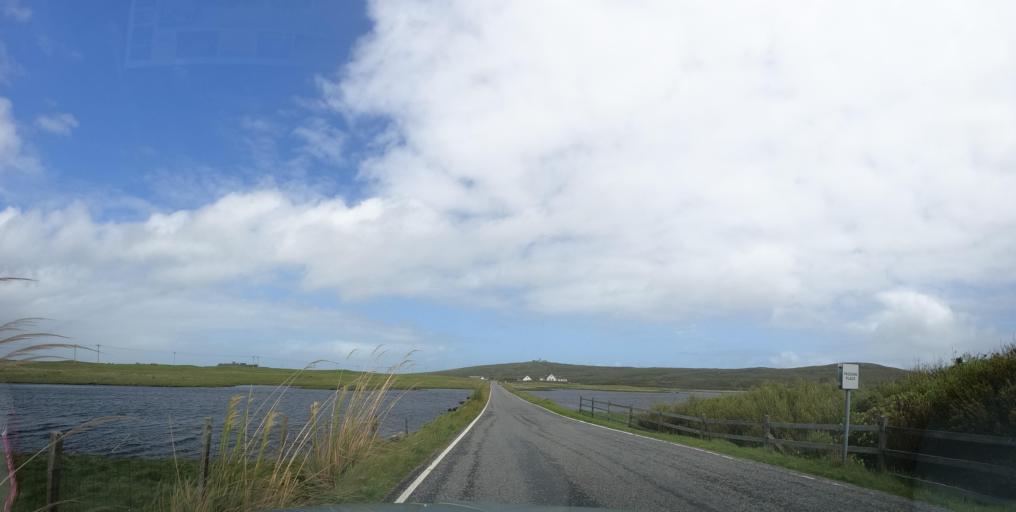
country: GB
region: Scotland
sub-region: Eilean Siar
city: Isle of South Uist
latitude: 57.3266
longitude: -7.3659
